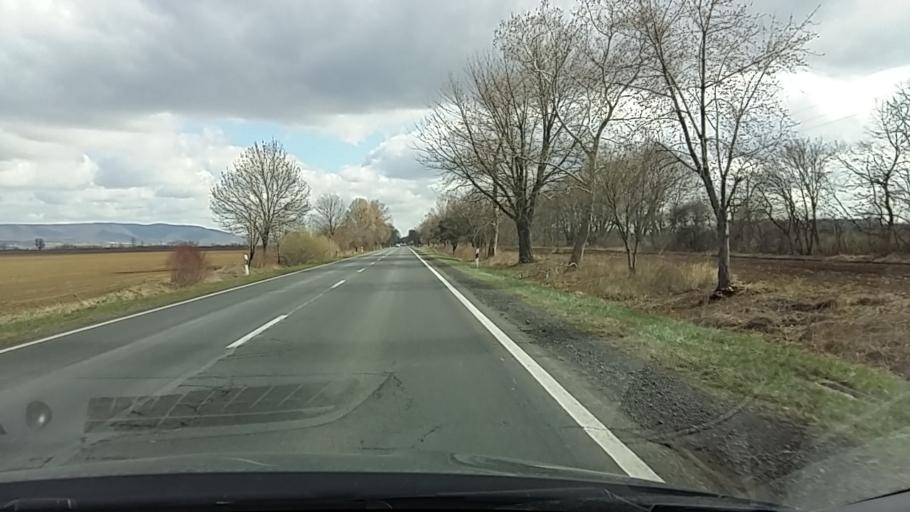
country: HU
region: Baranya
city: Szentlorinc
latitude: 46.0449
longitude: 18.0108
